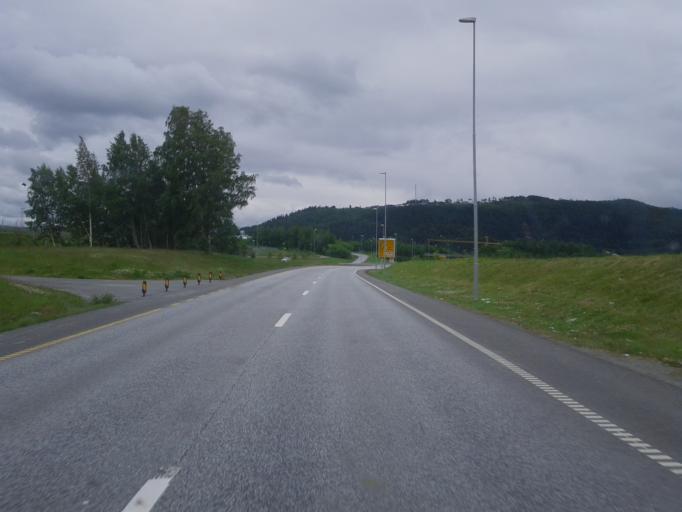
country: NO
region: Nord-Trondelag
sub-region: Stjordal
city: Stjordal
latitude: 63.4553
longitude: 10.9094
